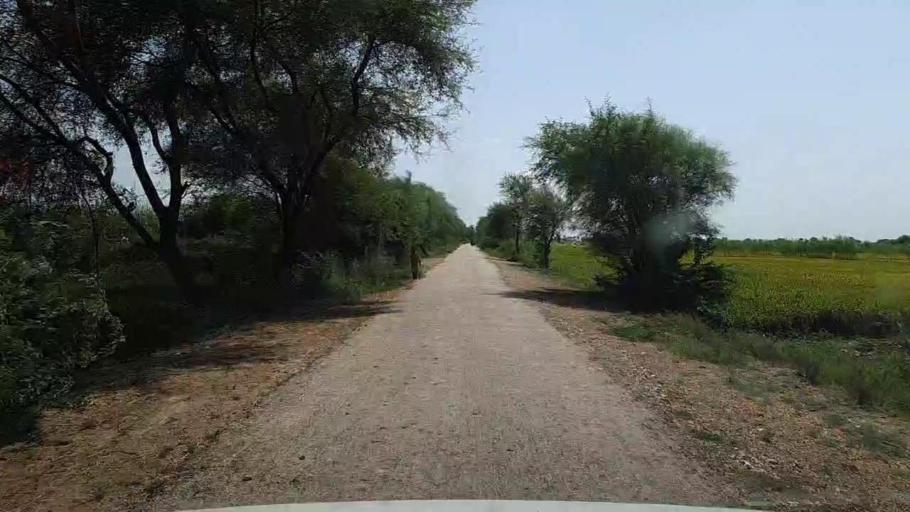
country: PK
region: Sindh
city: Kario
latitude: 24.6521
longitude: 68.5640
